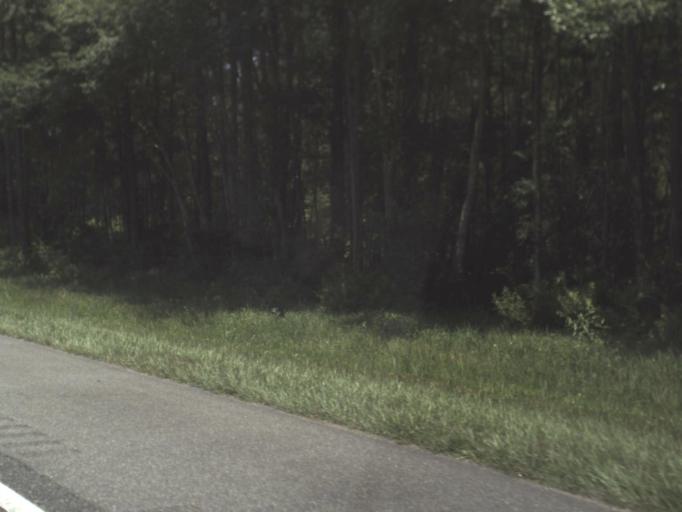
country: US
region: Florida
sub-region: Columbia County
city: Watertown
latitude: 30.2510
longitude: -82.5228
